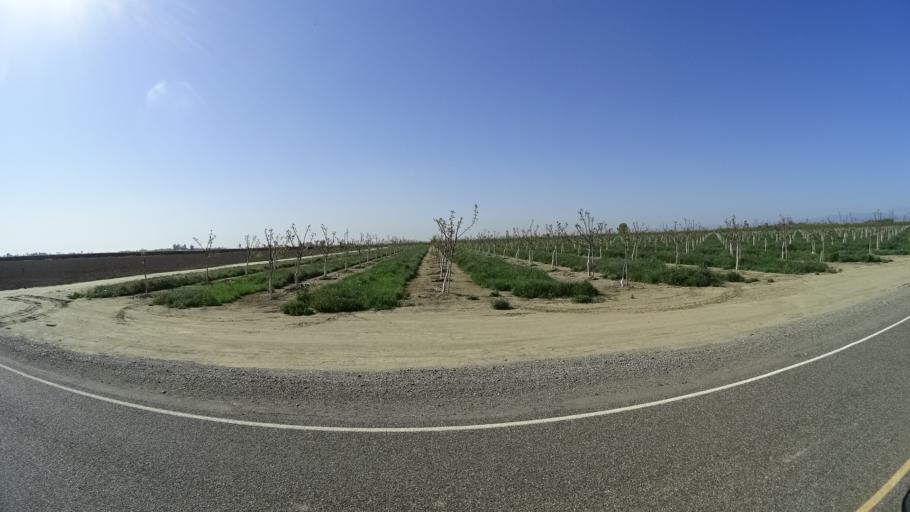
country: US
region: California
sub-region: Glenn County
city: Willows
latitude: 39.5533
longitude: -122.1466
